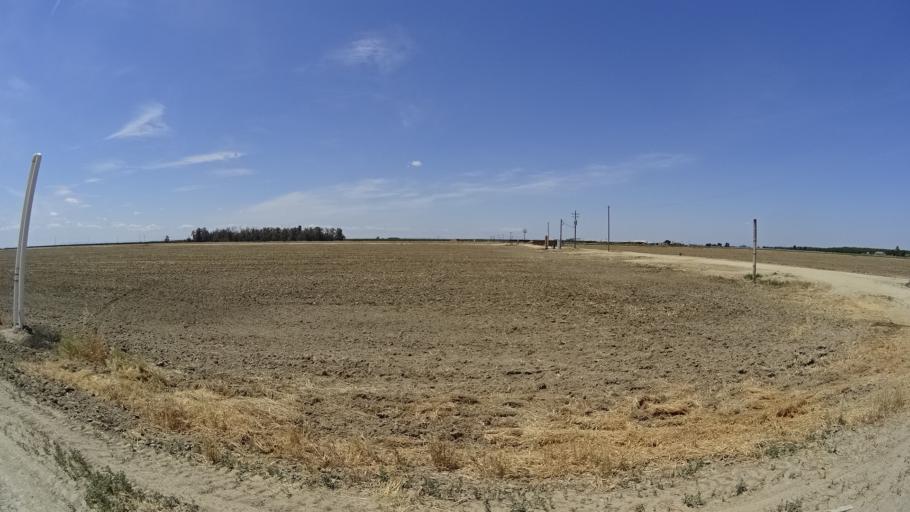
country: US
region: California
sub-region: Kings County
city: Home Garden
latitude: 36.2617
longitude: -119.6728
